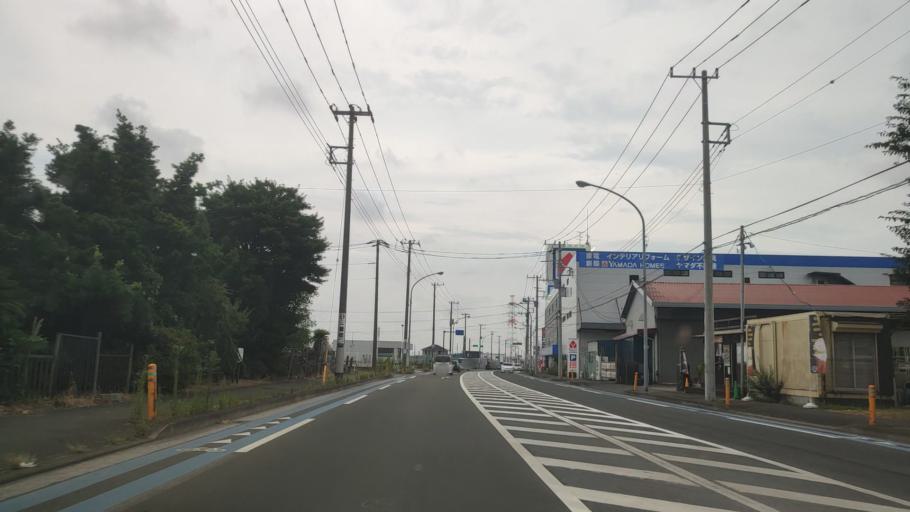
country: JP
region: Kanagawa
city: Minami-rinkan
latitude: 35.4358
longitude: 139.4846
